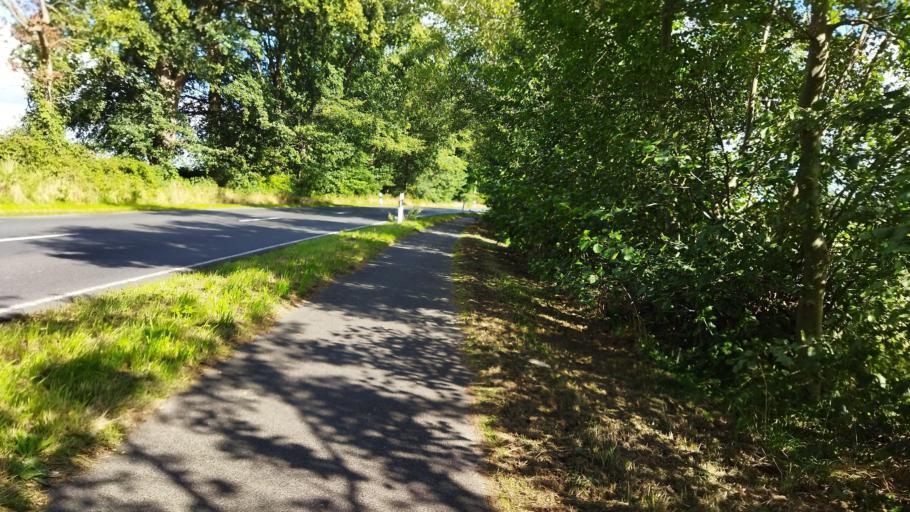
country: DE
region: Lower Saxony
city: Emsburen
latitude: 52.4011
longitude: 7.3222
